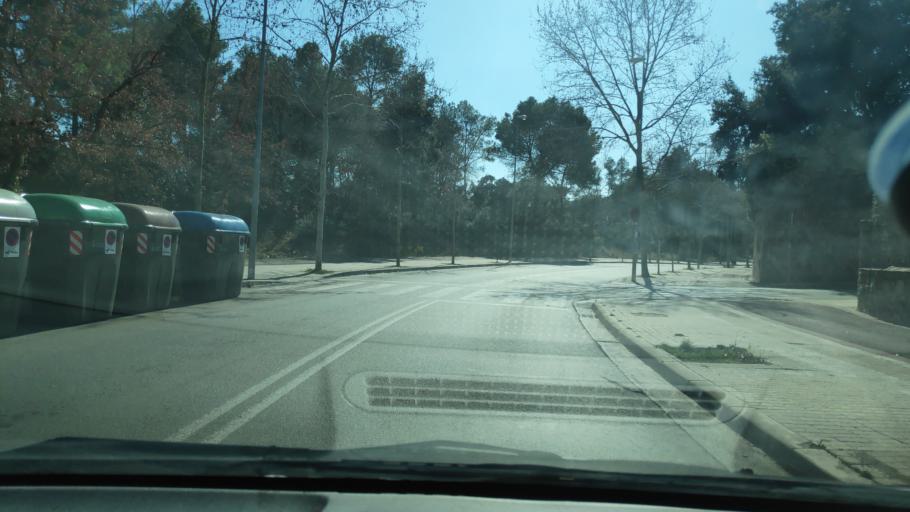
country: ES
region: Catalonia
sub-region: Provincia de Barcelona
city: Sant Quirze del Valles
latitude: 41.5565
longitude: 2.0722
